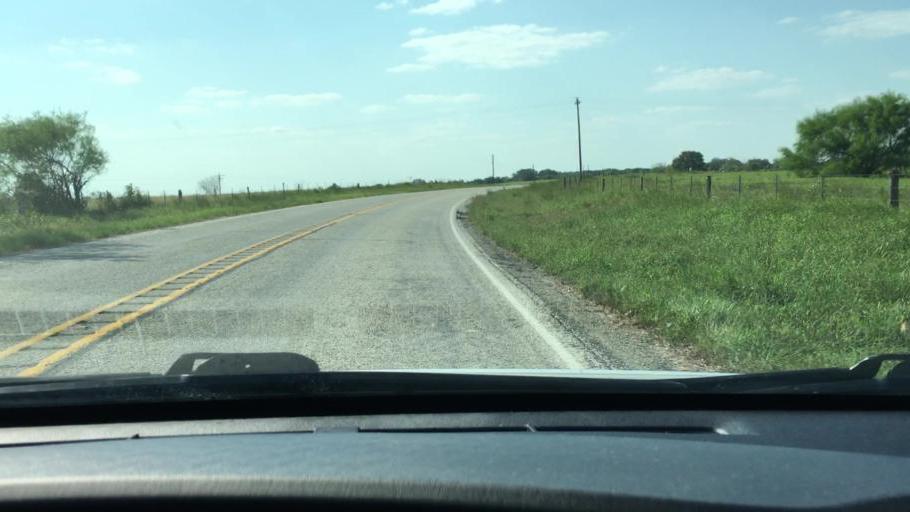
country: US
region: Texas
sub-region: DeWitt County
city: Yorktown
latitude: 28.9237
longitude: -97.3529
